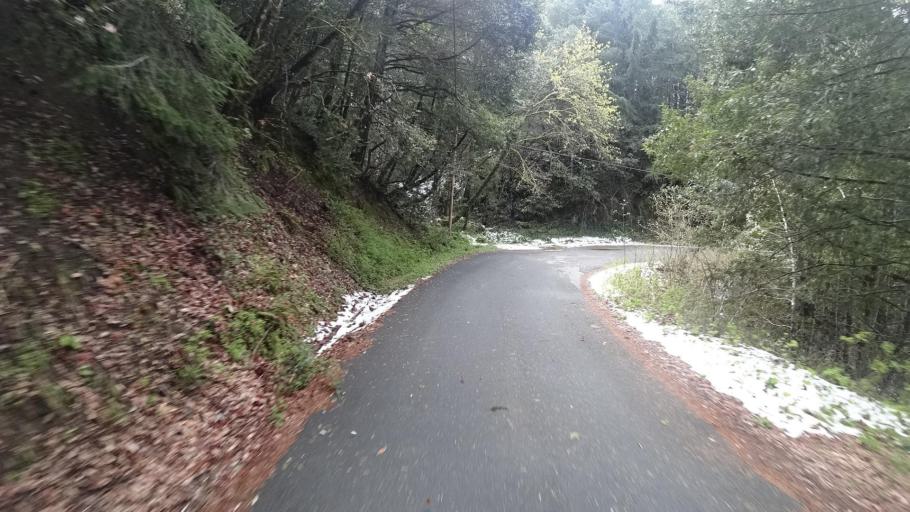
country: US
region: California
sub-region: Humboldt County
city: Blue Lake
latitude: 40.8764
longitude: -123.8805
